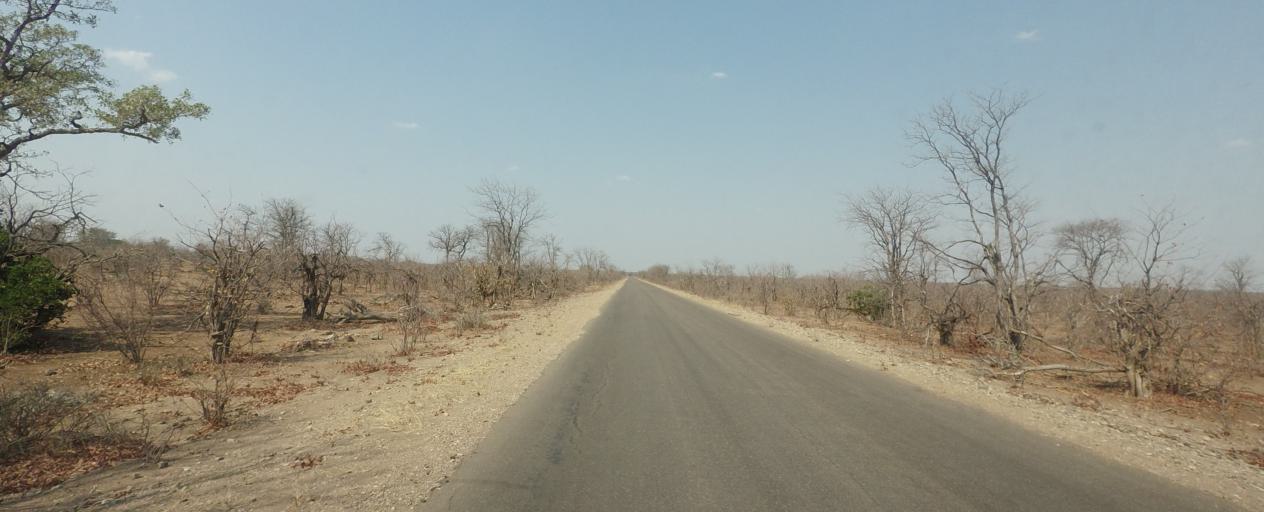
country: ZA
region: Limpopo
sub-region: Mopani District Municipality
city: Giyani
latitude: -23.1683
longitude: 31.3373
